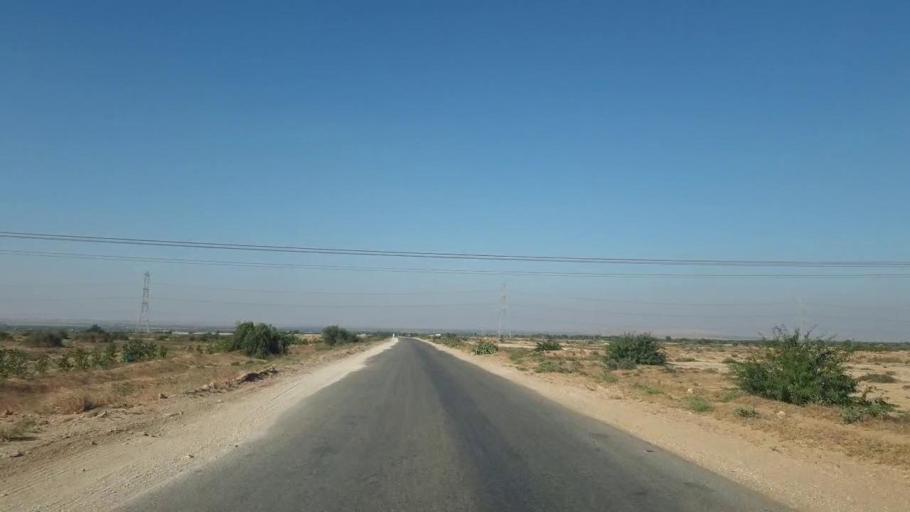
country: PK
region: Sindh
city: Gharo
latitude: 25.1747
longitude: 67.6599
